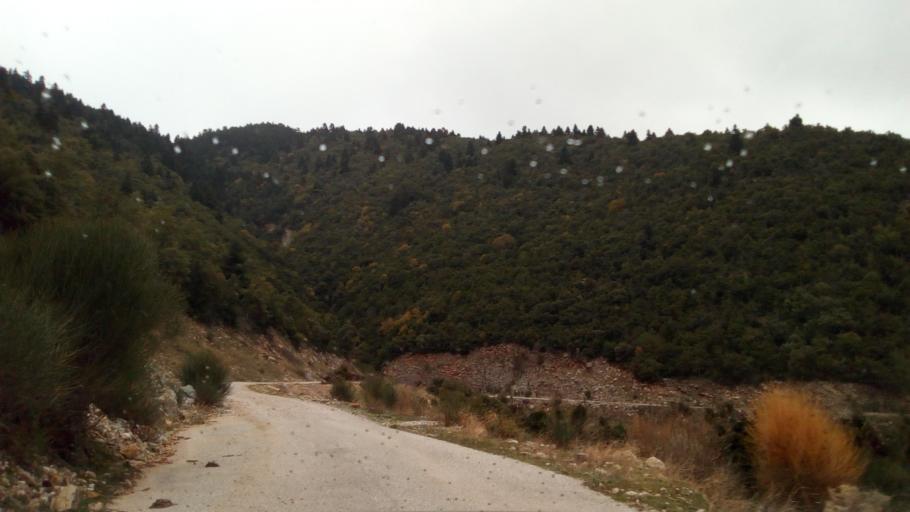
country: GR
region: West Greece
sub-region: Nomos Aitolias kai Akarnanias
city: Thermo
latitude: 38.6157
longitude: 21.8298
